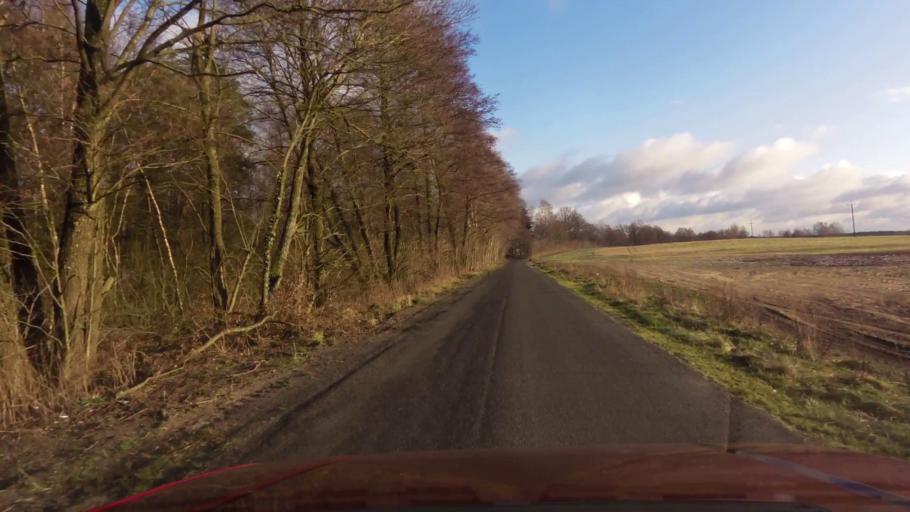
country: PL
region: West Pomeranian Voivodeship
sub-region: Koszalin
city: Koszalin
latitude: 54.0697
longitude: 16.1535
